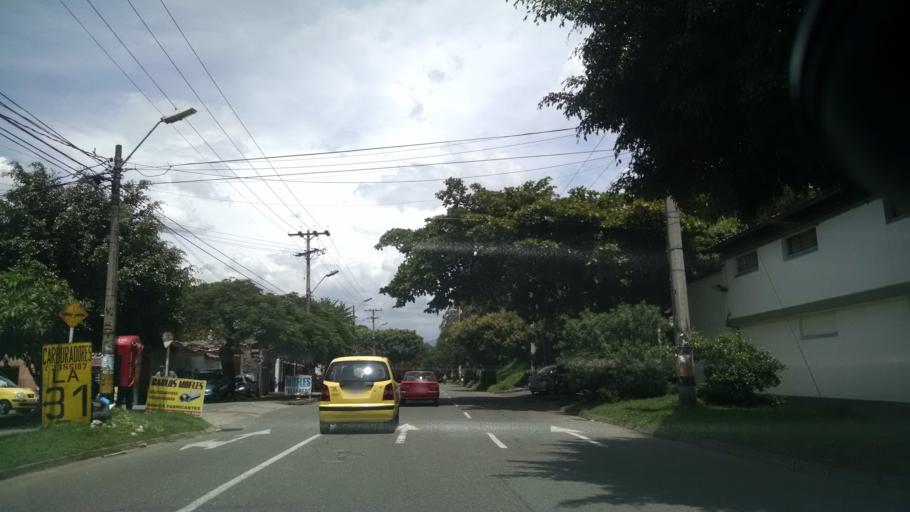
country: CO
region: Antioquia
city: Medellin
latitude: 6.2338
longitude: -75.5827
